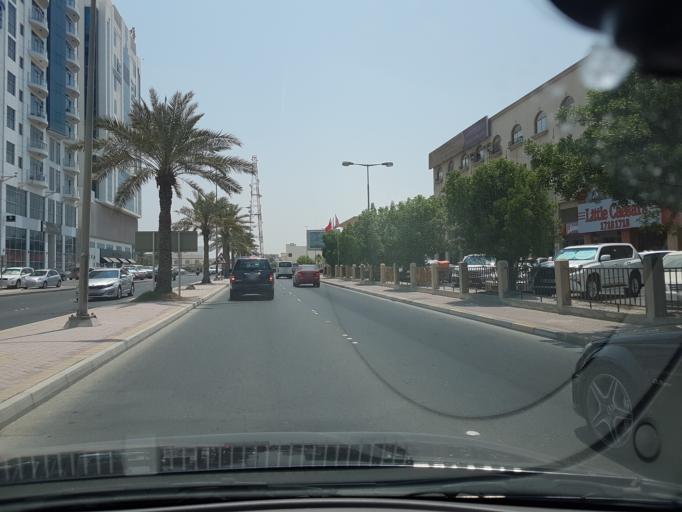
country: BH
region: Manama
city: Manama
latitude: 26.2059
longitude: 50.5756
